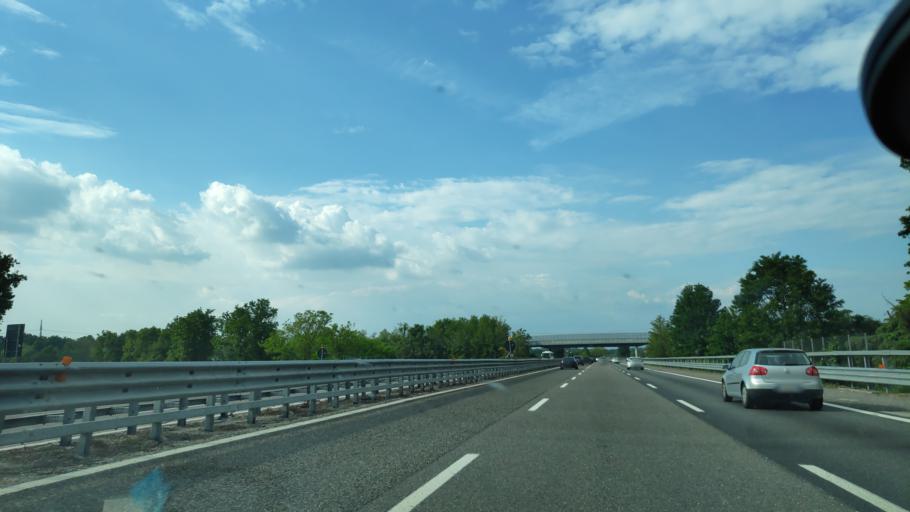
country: IT
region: Lombardy
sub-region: Provincia di Pavia
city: Zerbolo
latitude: 45.2142
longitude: 9.0174
